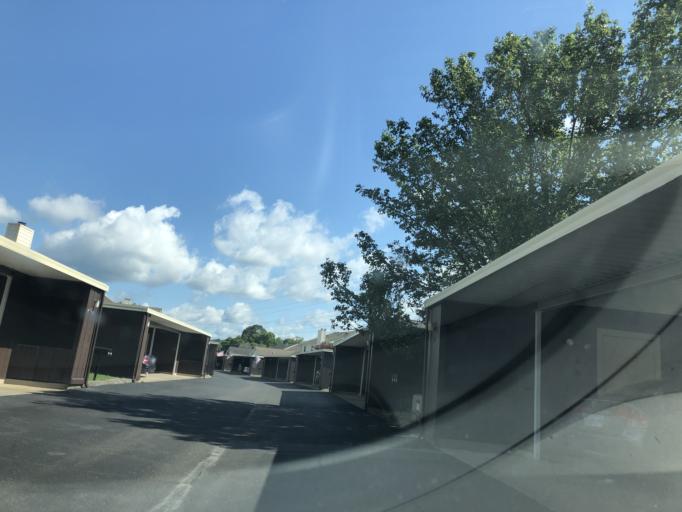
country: US
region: Tennessee
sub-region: Davidson County
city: Belle Meade
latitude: 36.0703
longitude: -86.9522
